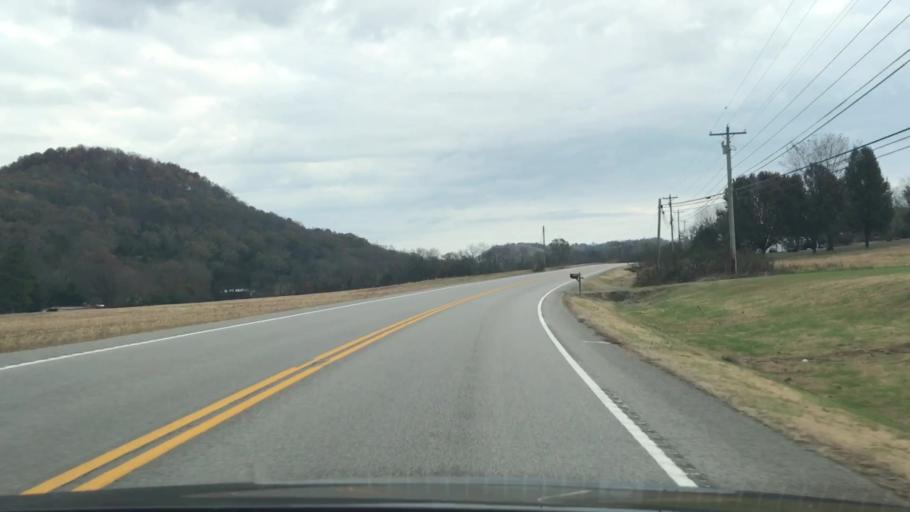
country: US
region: Tennessee
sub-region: Macon County
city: Lafayette
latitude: 36.4430
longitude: -86.0636
